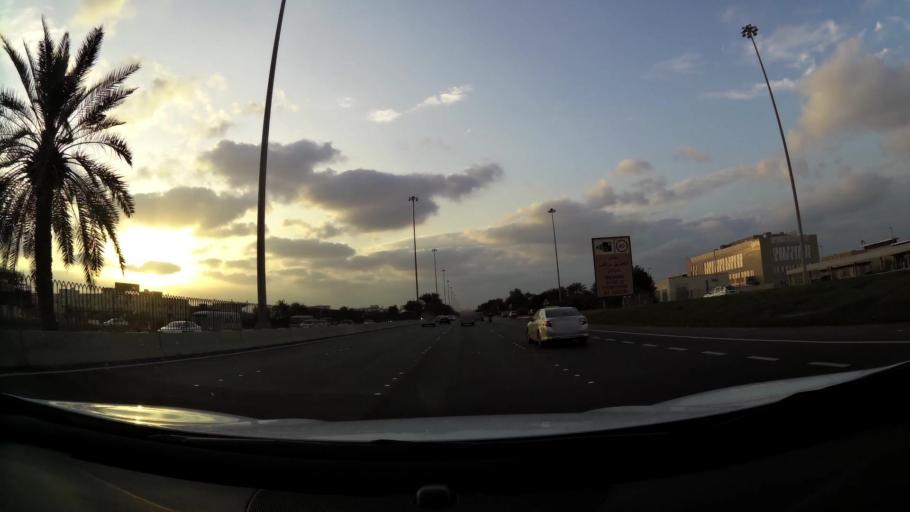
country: AE
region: Abu Dhabi
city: Abu Dhabi
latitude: 24.4162
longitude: 54.5006
